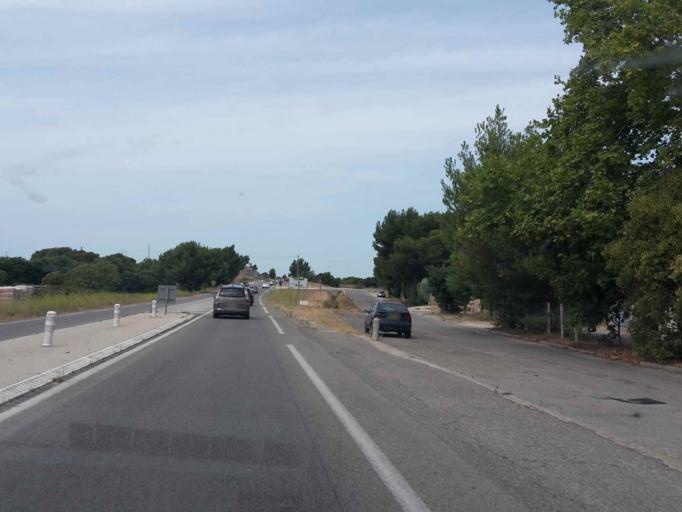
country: FR
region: Provence-Alpes-Cote d'Azur
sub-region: Departement des Bouches-du-Rhone
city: Lancon-Provence
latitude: 43.5880
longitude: 5.1227
